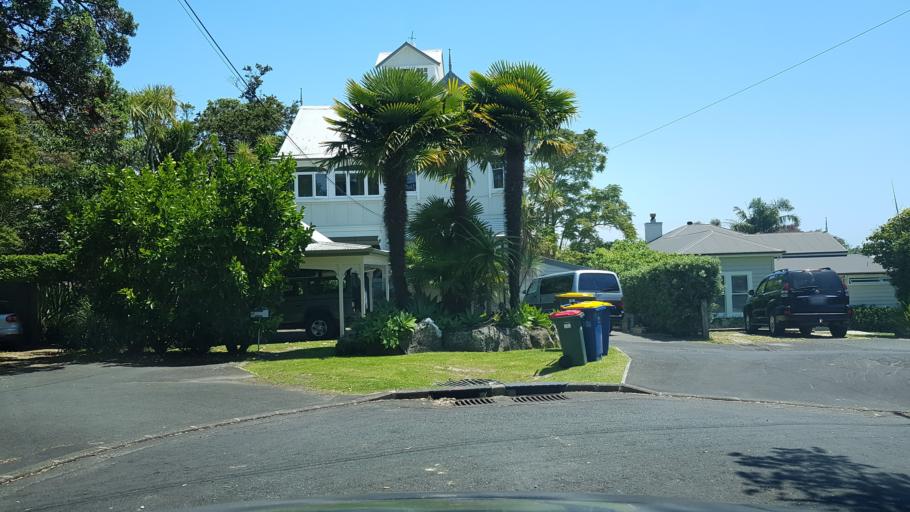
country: NZ
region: Auckland
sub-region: Auckland
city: North Shore
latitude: -36.8259
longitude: 174.7748
